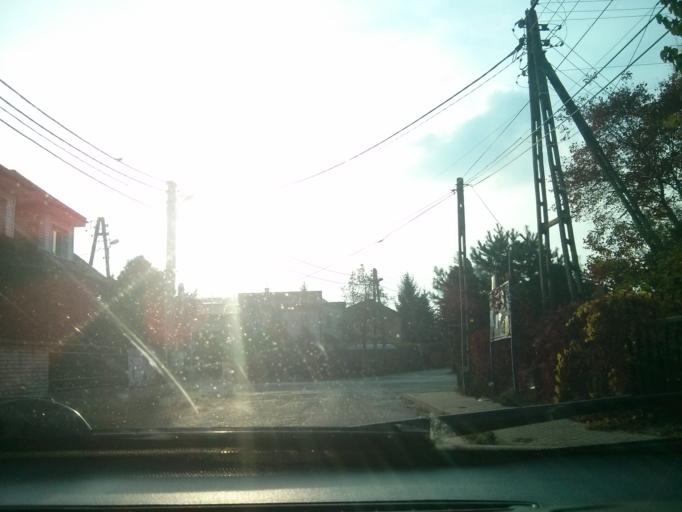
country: PL
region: Masovian Voivodeship
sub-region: Powiat piaseczynski
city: Konstancin-Jeziorna
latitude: 52.1086
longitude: 21.1305
